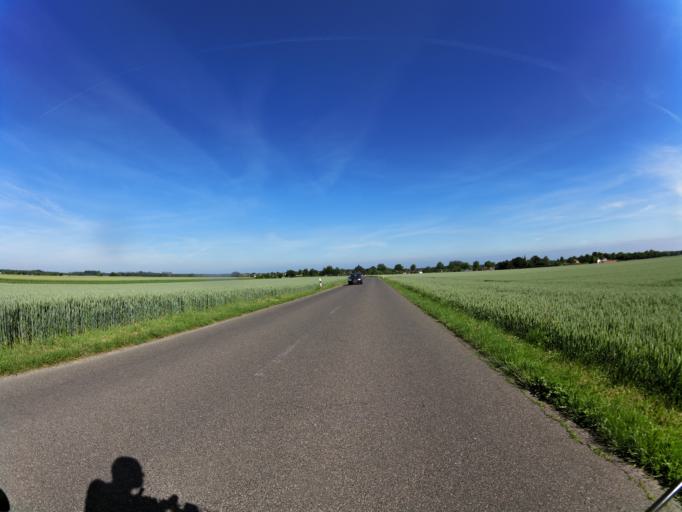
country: DE
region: North Rhine-Westphalia
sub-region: Regierungsbezirk Koln
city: Ubach-Palenberg
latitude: 50.9340
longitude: 6.0687
